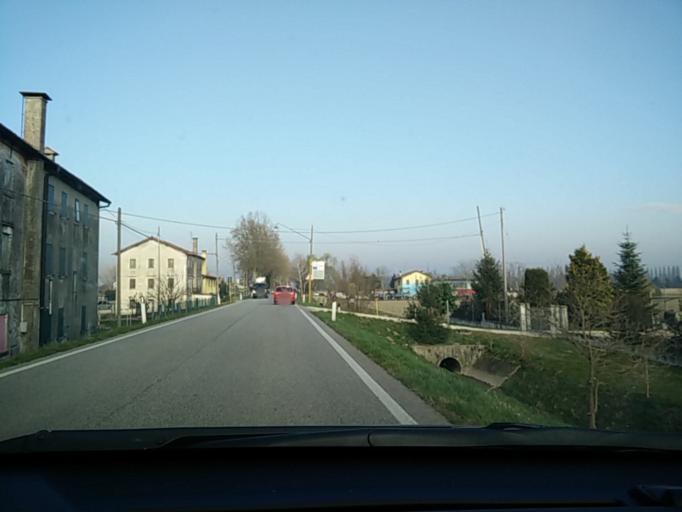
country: IT
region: Veneto
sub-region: Provincia di Treviso
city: Zenson di Piave
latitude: 45.6844
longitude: 12.4713
